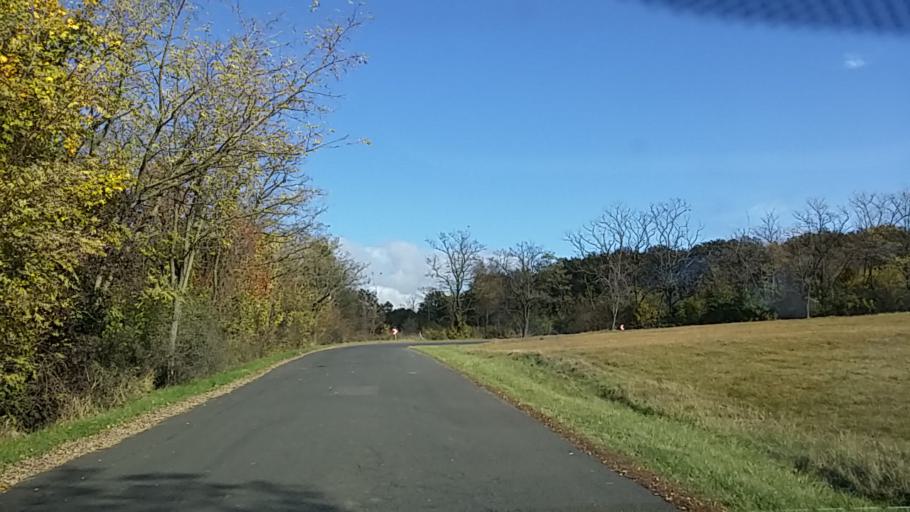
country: HU
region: Borsod-Abauj-Zemplen
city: Gonc
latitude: 48.3840
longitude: 21.3118
